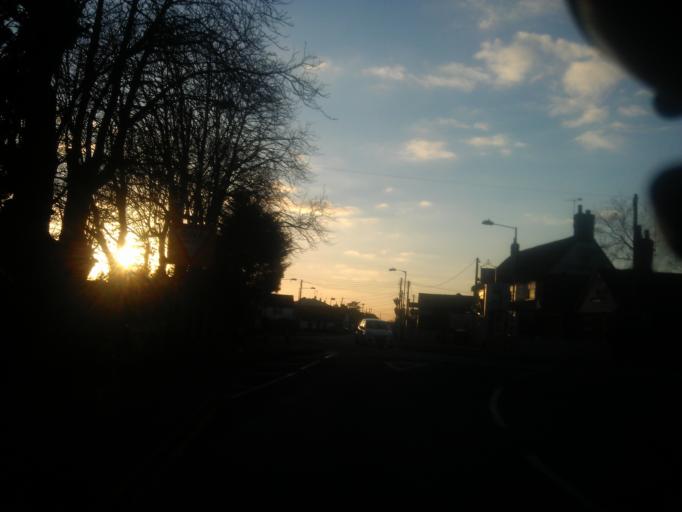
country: GB
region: England
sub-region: Essex
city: Hatfield Peverel
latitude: 51.7775
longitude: 0.6000
